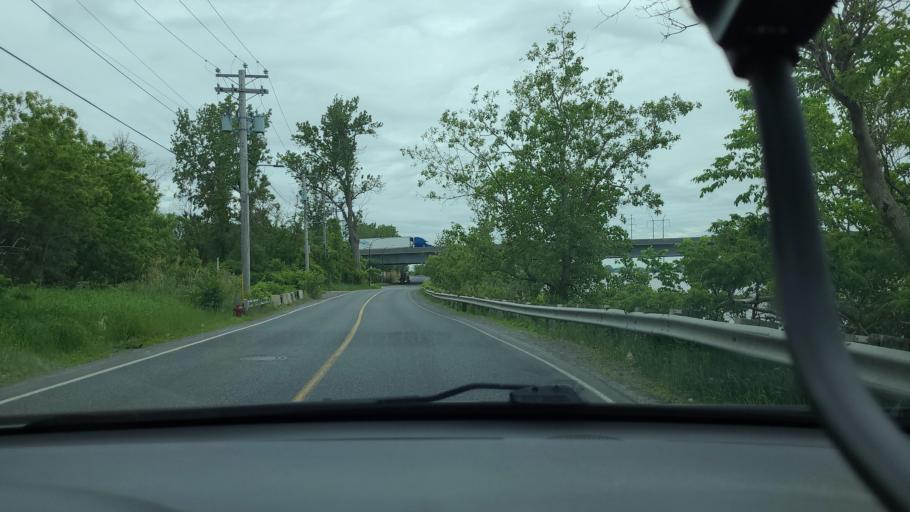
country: CA
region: Quebec
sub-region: Lanaudiere
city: Charlemagne
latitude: 45.6994
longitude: -73.5066
